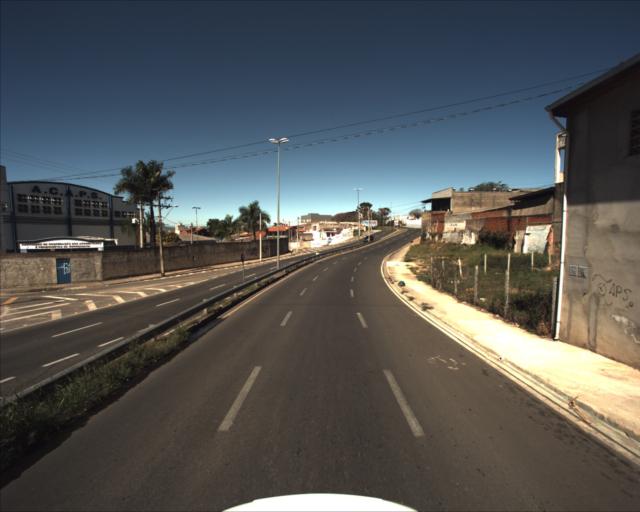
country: BR
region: Sao Paulo
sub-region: Sorocaba
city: Sorocaba
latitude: -23.4998
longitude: -47.4822
